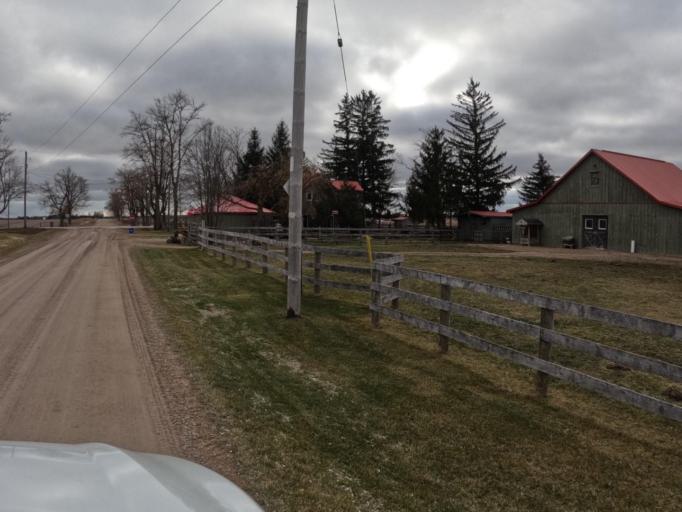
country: CA
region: Ontario
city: Shelburne
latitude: 43.8813
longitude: -80.4043
